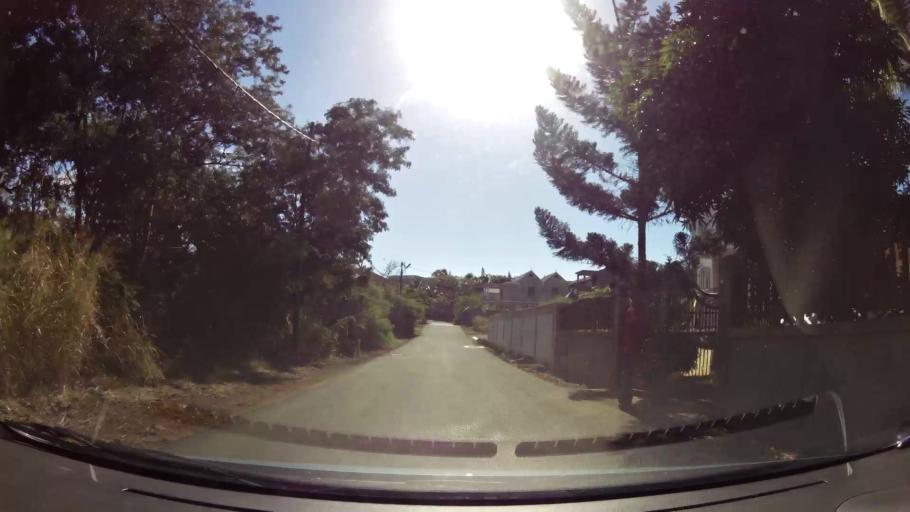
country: MU
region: Black River
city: Flic en Flac
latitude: -20.2712
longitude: 57.3748
